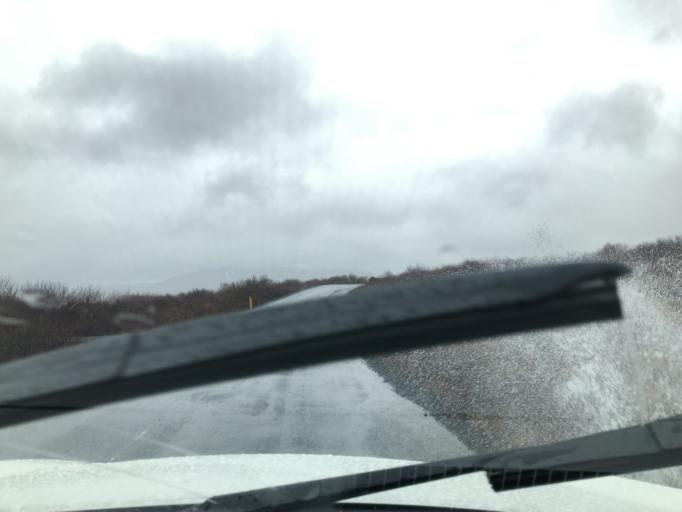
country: IS
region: South
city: Hveragerdi
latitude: 64.2464
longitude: -21.0244
